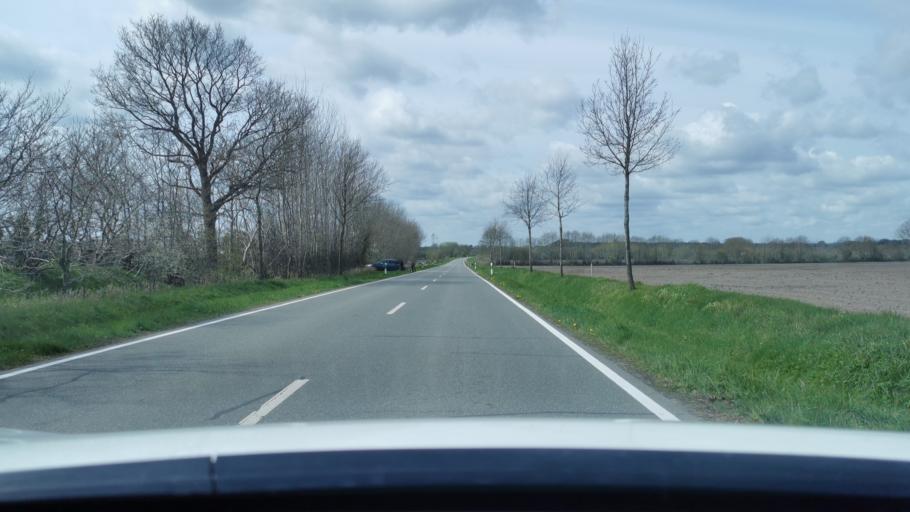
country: DE
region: Schleswig-Holstein
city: Breiholz
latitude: 54.1988
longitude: 9.5111
